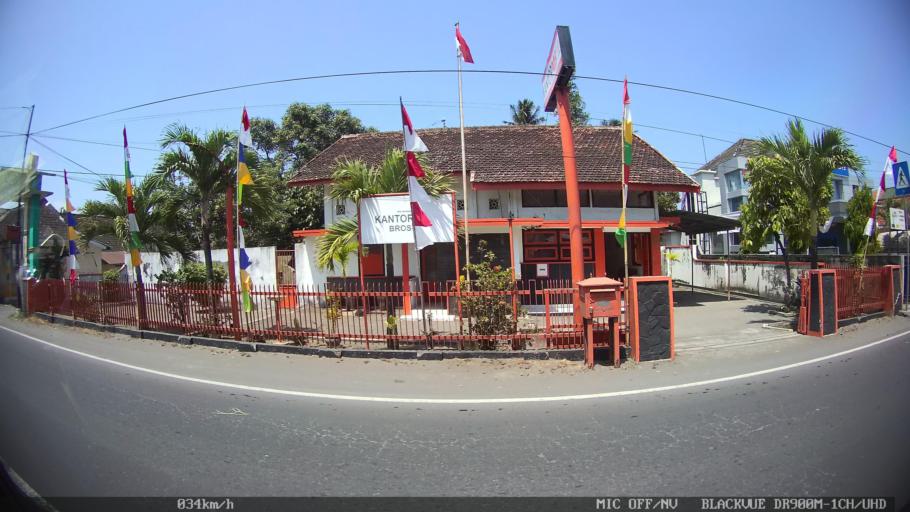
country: ID
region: Daerah Istimewa Yogyakarta
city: Srandakan
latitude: -7.9403
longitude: 110.2373
